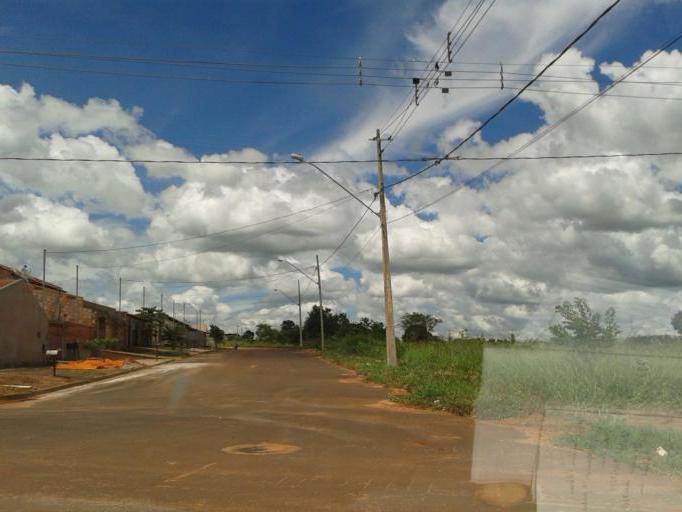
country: BR
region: Minas Gerais
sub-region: Santa Vitoria
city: Santa Vitoria
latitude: -18.8487
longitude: -50.1358
